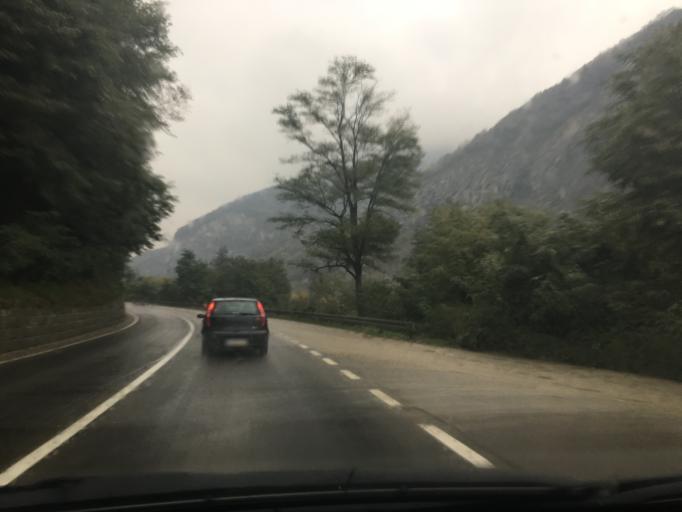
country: RS
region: Central Serbia
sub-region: Pcinjski Okrug
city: Vladicin Han
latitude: 42.7530
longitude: 22.0814
